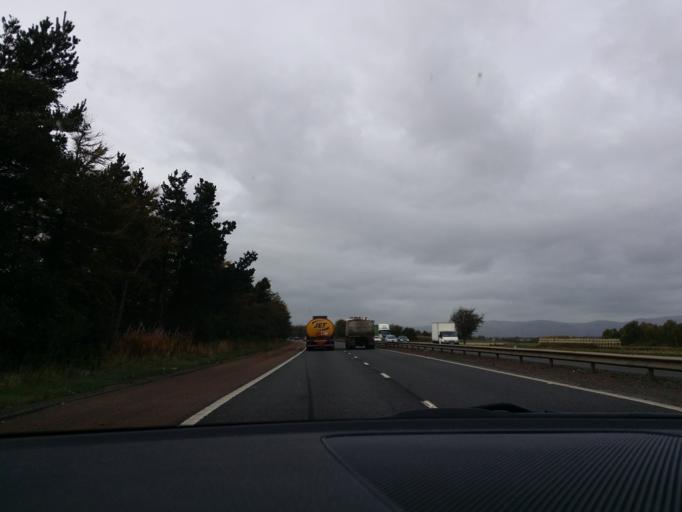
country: GB
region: Scotland
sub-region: Falkirk
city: Airth
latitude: 56.0351
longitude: -3.7684
